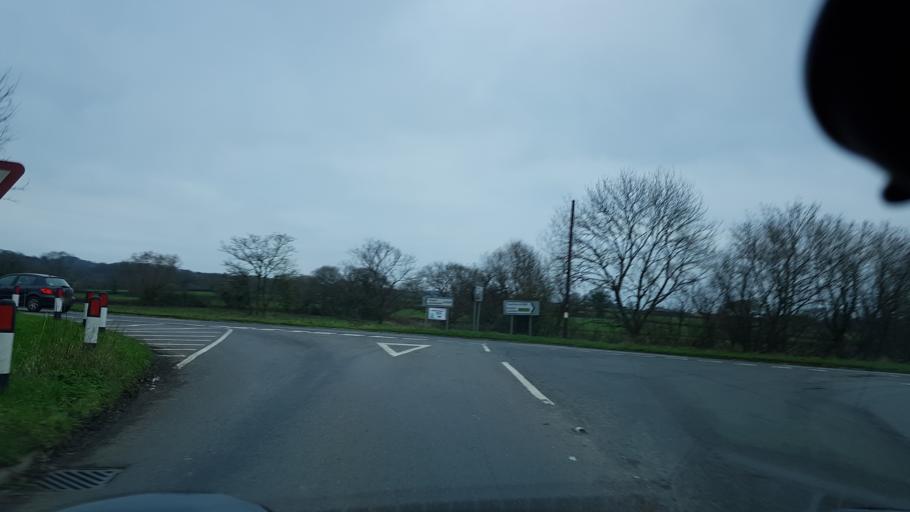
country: GB
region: England
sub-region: Somerset
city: Ilminster
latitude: 50.9117
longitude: -2.9389
